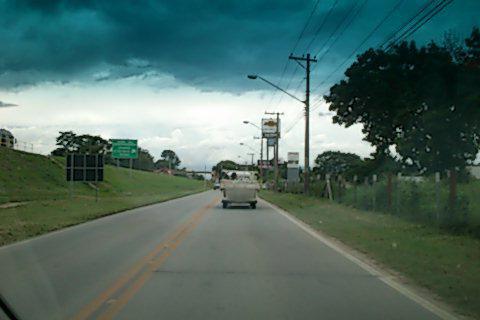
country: BR
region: Sao Paulo
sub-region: Jacarei
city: Jacarei
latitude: -23.2769
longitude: -45.9765
